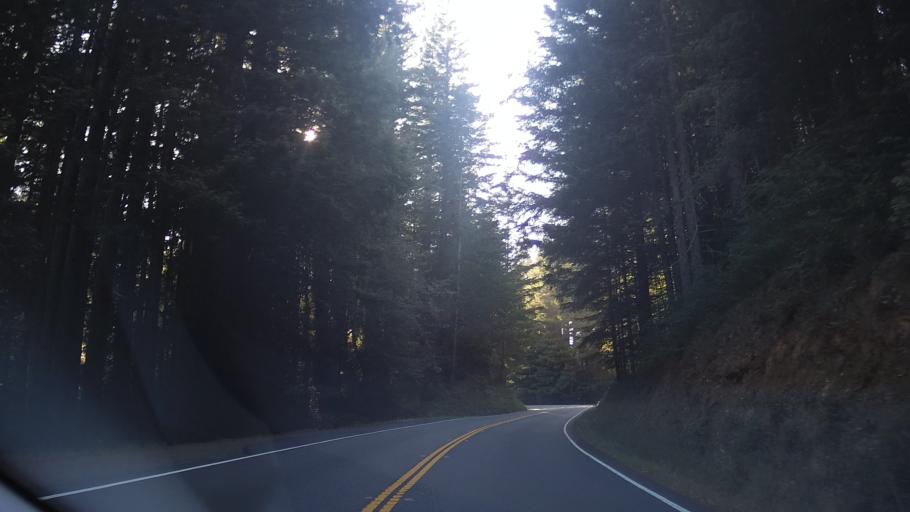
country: US
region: California
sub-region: Mendocino County
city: Fort Bragg
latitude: 39.3648
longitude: -123.6718
